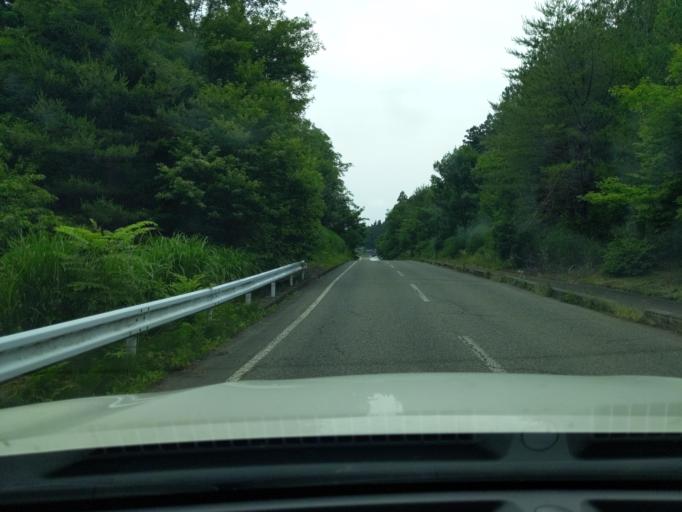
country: JP
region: Niigata
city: Kashiwazaki
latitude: 37.3407
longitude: 138.5847
